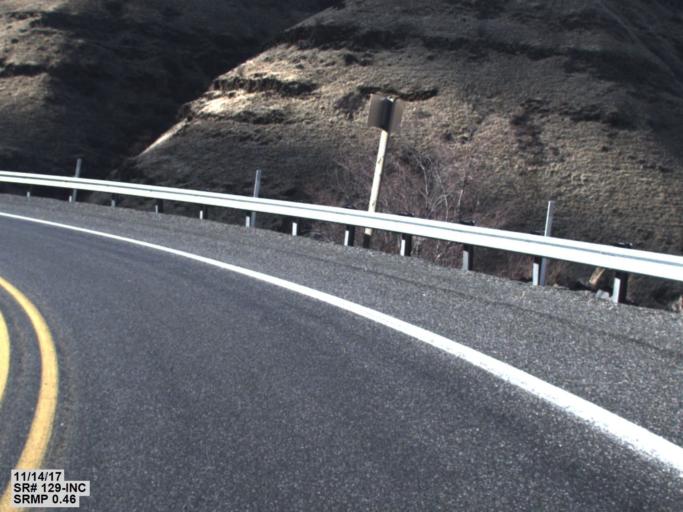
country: US
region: Washington
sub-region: Asotin County
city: Asotin
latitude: 46.0044
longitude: -117.2774
